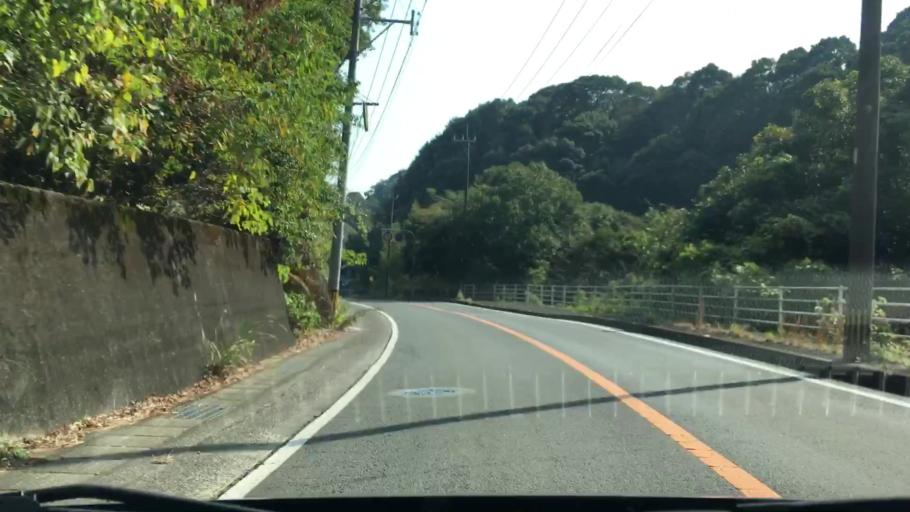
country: JP
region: Nagasaki
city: Togitsu
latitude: 32.9570
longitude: 129.7830
